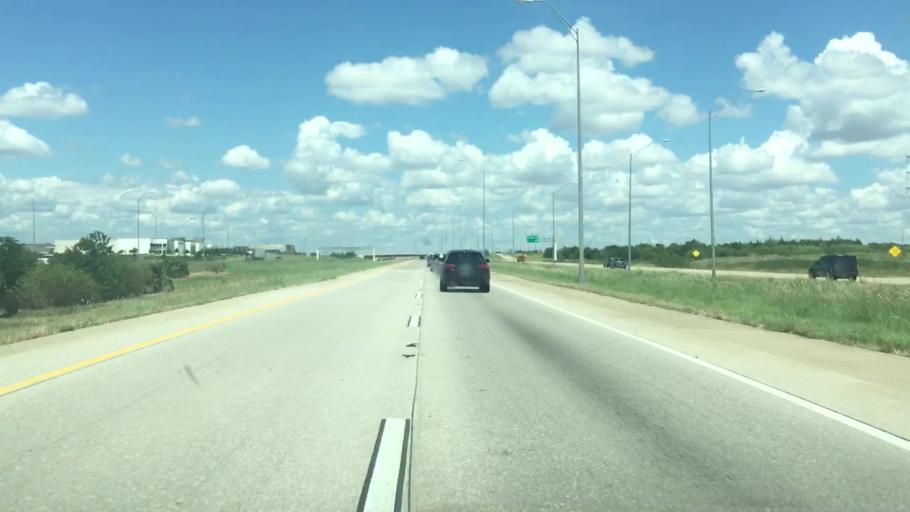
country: US
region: Texas
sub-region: Travis County
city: Pflugerville
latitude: 30.4147
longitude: -97.5854
